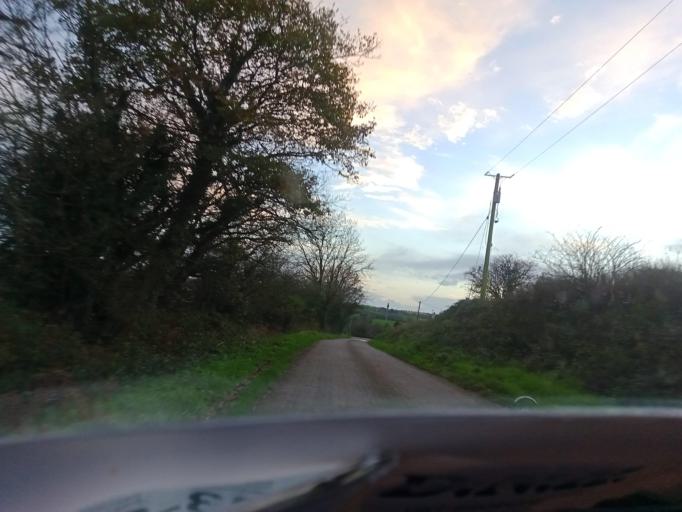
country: IE
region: Leinster
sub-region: Loch Garman
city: New Ross
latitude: 52.3361
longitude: -7.0131
